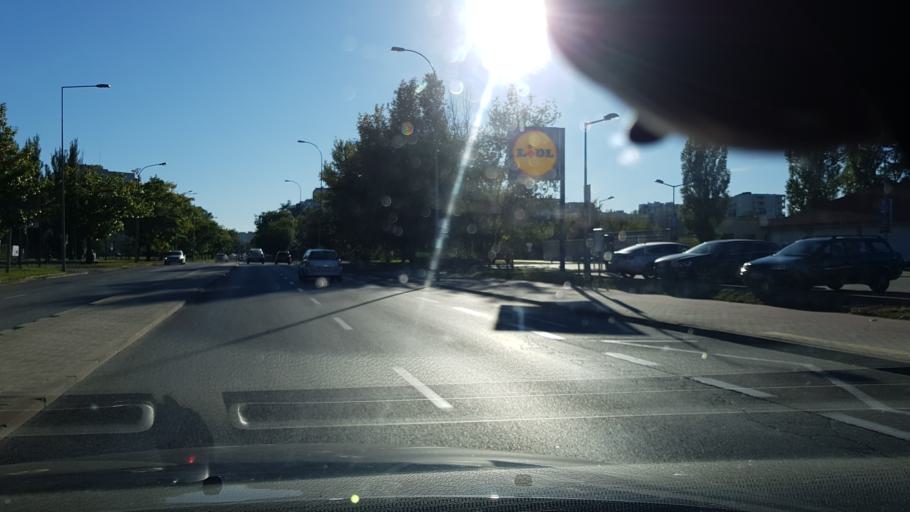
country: PL
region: Masovian Voivodeship
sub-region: Warszawa
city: Bielany
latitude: 52.2885
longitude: 20.9330
